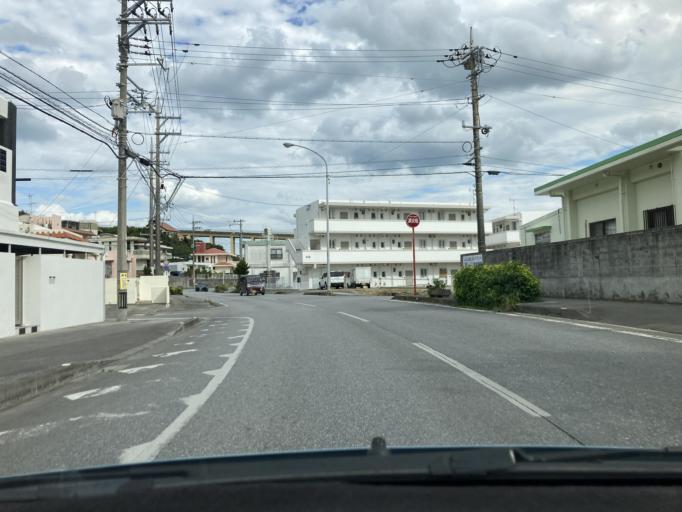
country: JP
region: Okinawa
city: Gushikawa
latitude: 26.3490
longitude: 127.8531
